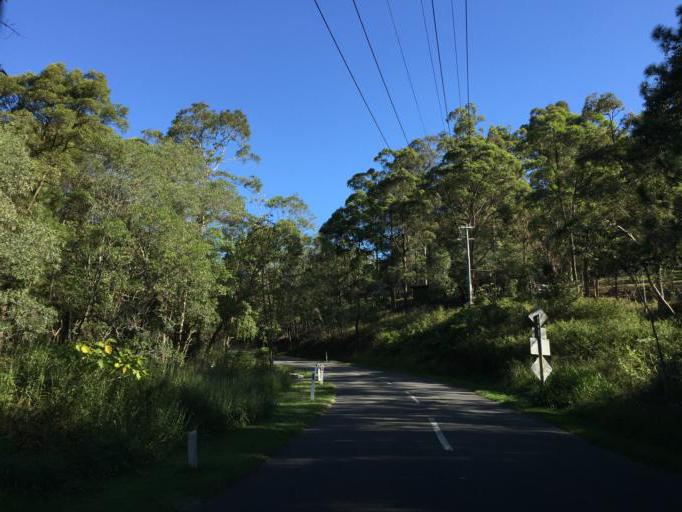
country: AU
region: Queensland
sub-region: Brisbane
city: Kenmore Hills
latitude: -27.4591
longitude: 152.9299
